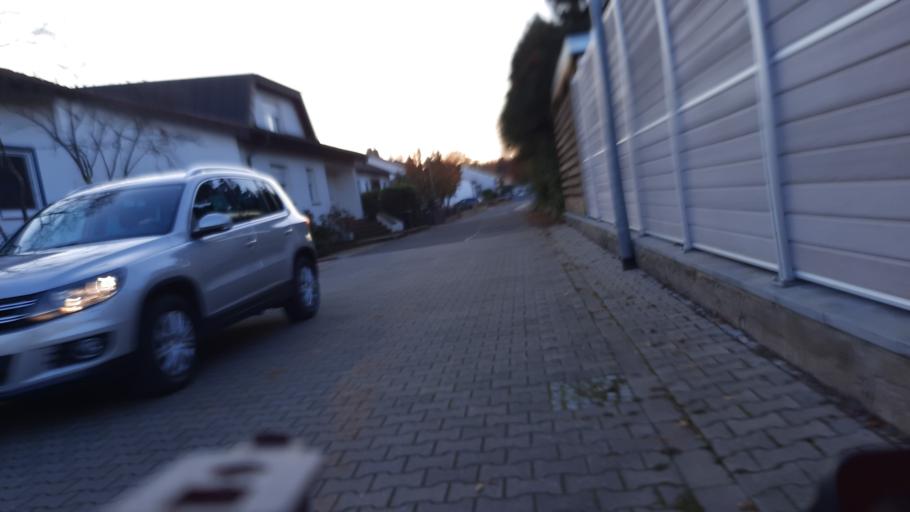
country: DE
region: Rheinland-Pfalz
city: Offstein
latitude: 49.6031
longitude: 8.2578
